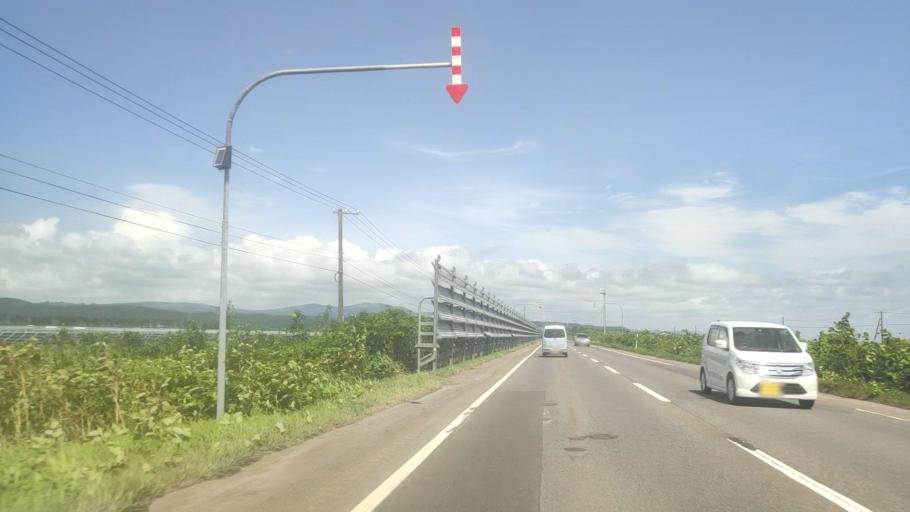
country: JP
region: Hokkaido
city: Nanae
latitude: 42.2994
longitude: 140.2719
